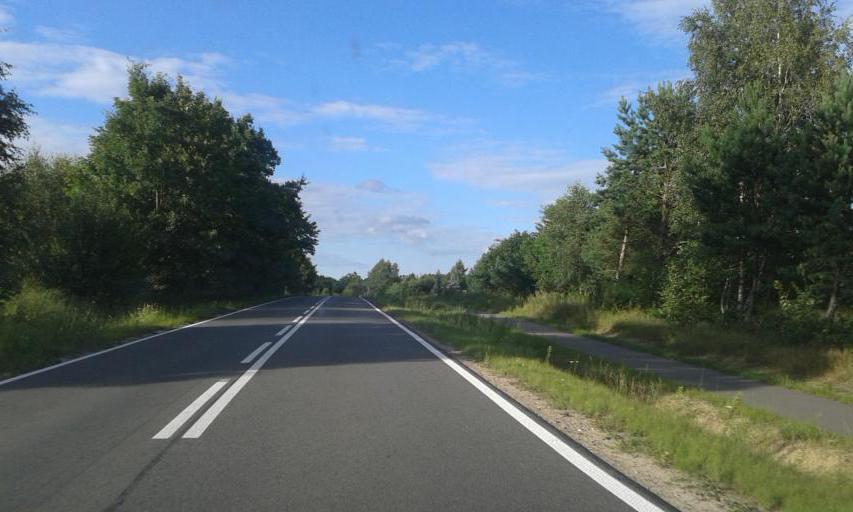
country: PL
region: West Pomeranian Voivodeship
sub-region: Koszalin
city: Koszalin
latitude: 54.1045
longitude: 16.1683
